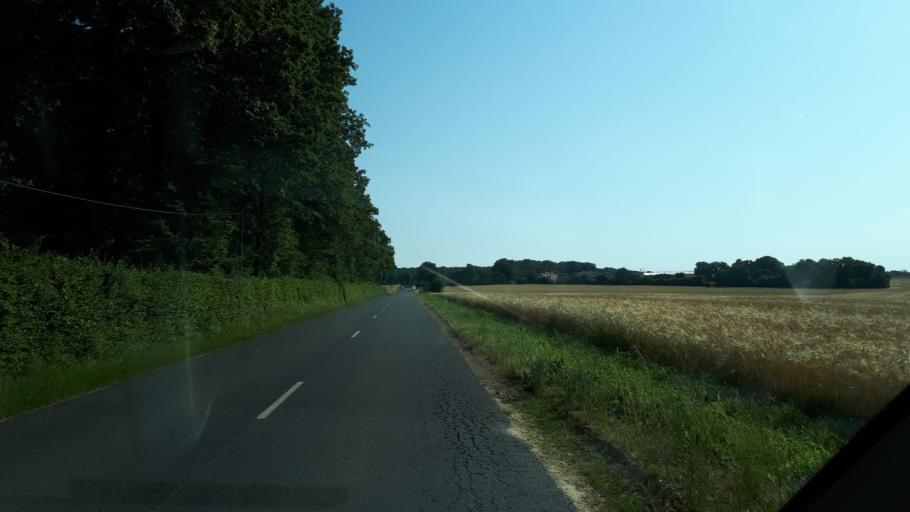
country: FR
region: Centre
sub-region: Departement du Loir-et-Cher
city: Droue
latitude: 48.0326
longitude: 1.0683
